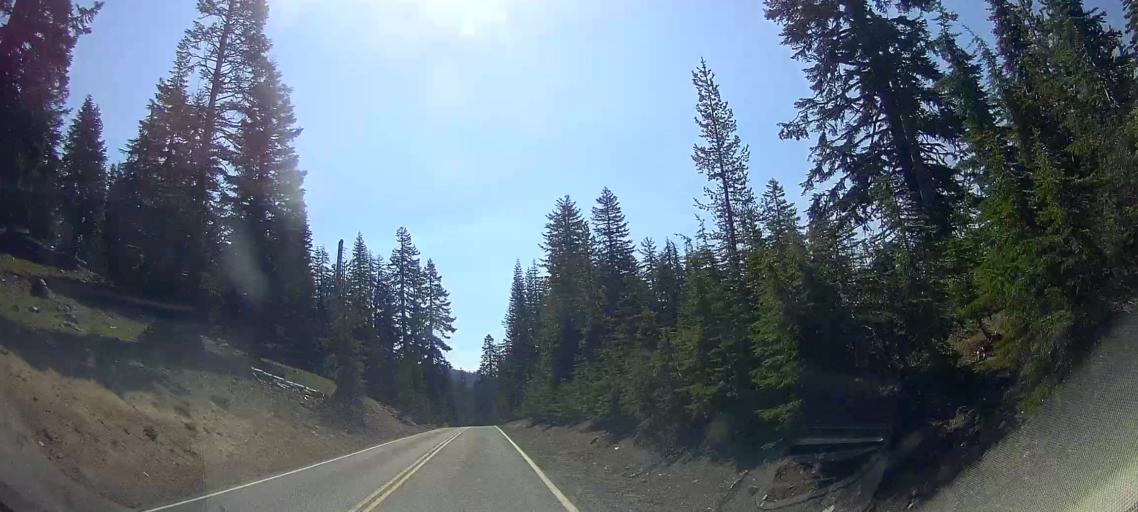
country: US
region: Oregon
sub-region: Klamath County
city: Klamath Falls
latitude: 42.8798
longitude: -122.1152
